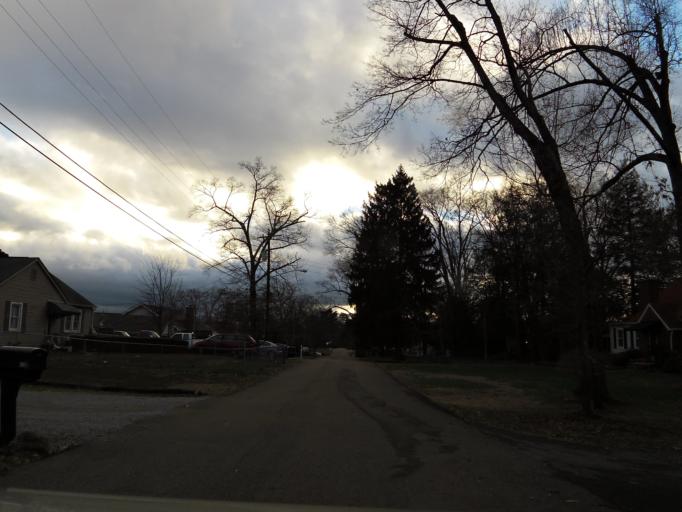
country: US
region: Tennessee
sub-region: Knox County
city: Knoxville
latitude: 36.0084
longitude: -83.9017
